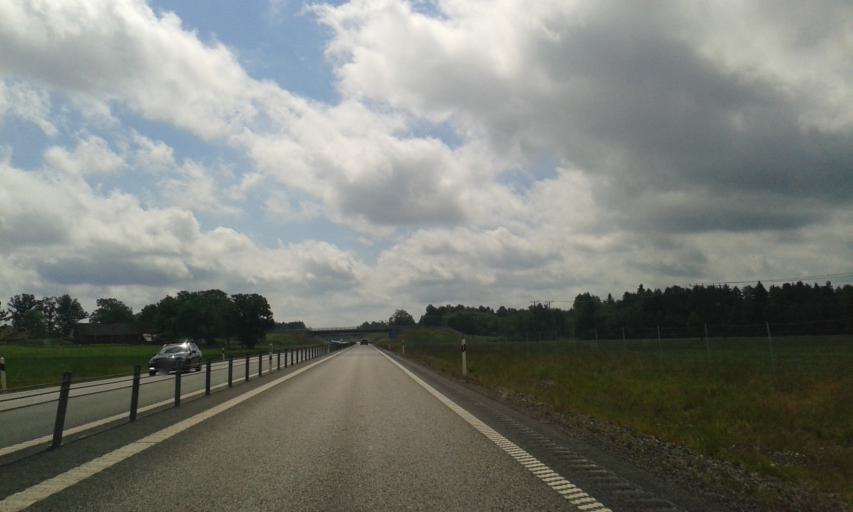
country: SE
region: Joenkoeping
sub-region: Gislaveds Kommun
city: Gislaved
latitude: 57.3067
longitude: 13.5781
